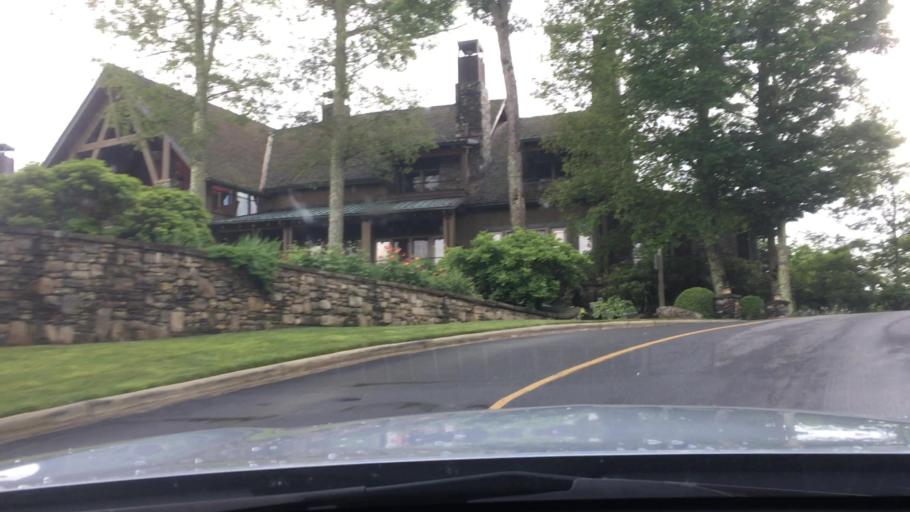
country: US
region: North Carolina
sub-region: Yancey County
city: Burnsville
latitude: 35.8713
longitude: -82.3467
